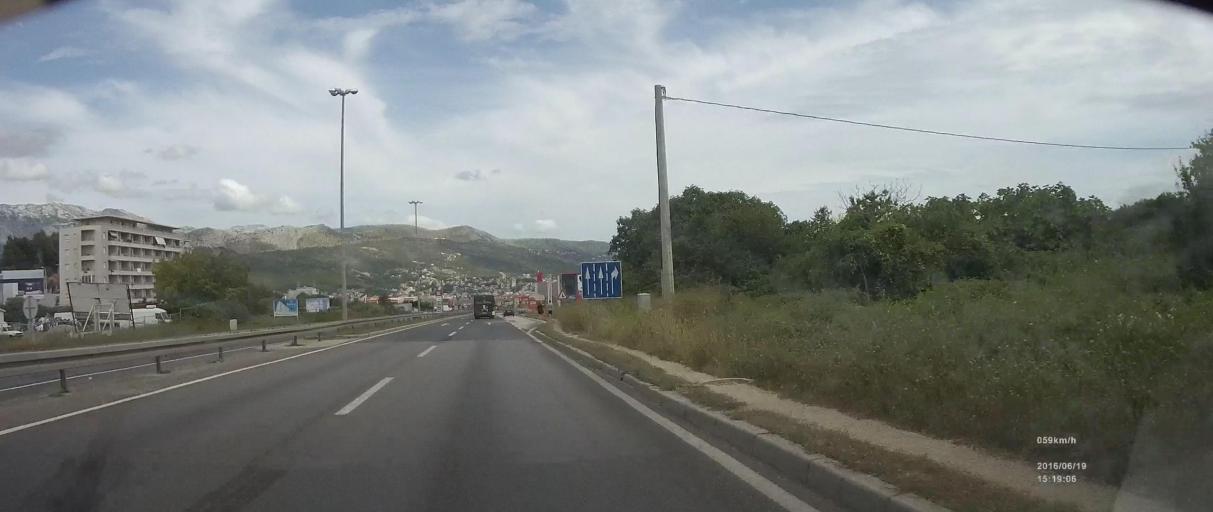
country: HR
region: Splitsko-Dalmatinska
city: Kamen
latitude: 43.5076
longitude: 16.5010
